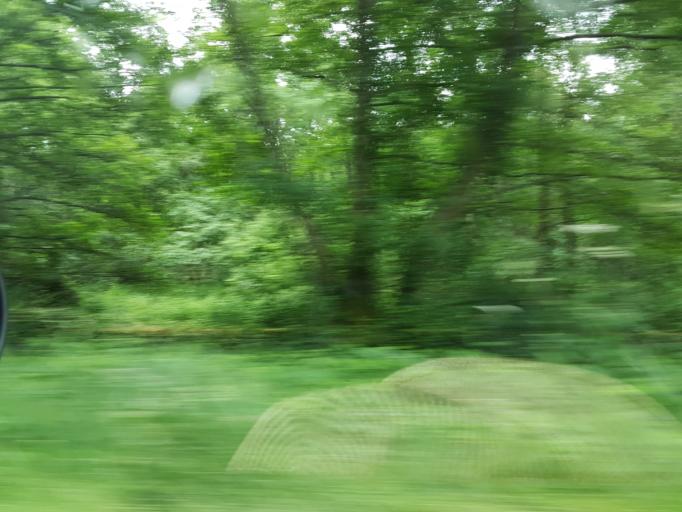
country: FR
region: Bourgogne
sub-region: Departement de la Nievre
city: Corbigny
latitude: 47.1764
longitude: 3.7470
